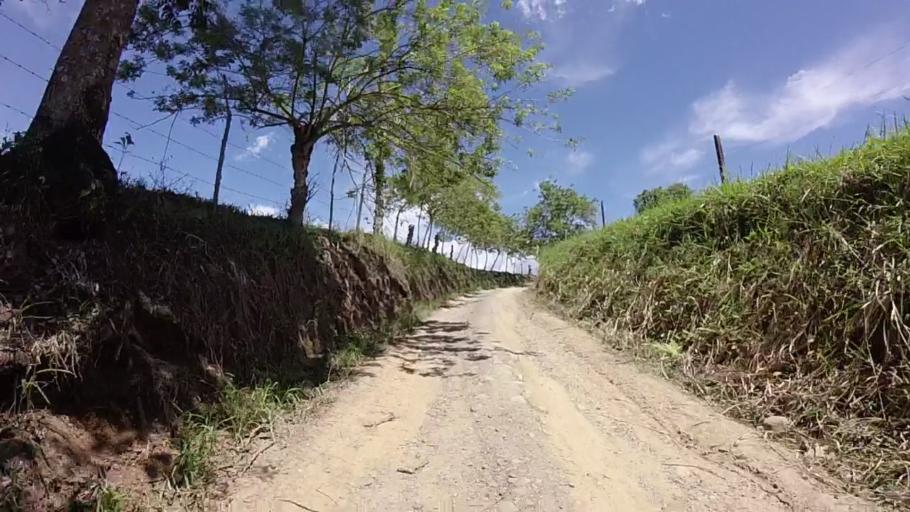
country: CO
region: Valle del Cauca
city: Alcala
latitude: 4.7114
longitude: -75.8070
